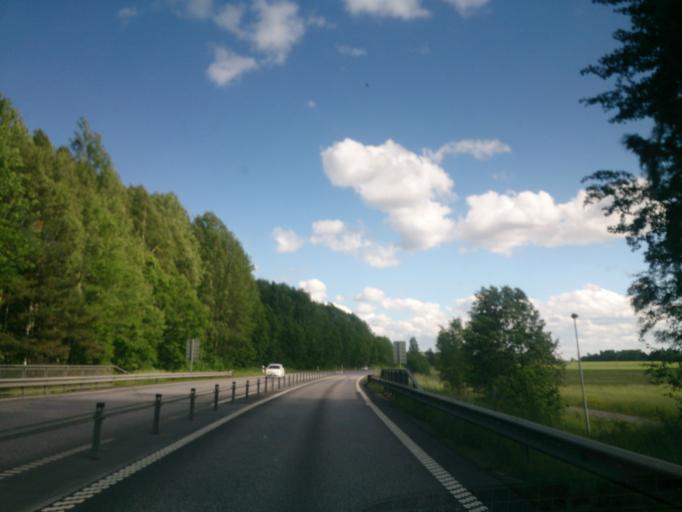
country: SE
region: OEstergoetland
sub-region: Norrkopings Kommun
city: Jursla
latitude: 58.6697
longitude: 16.1630
